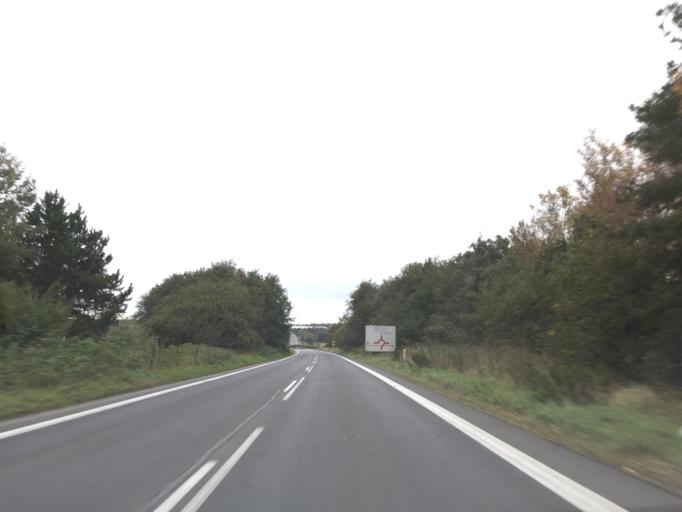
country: DK
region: Central Jutland
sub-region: Viborg Kommune
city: Bjerringbro
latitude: 56.3678
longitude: 9.6768
